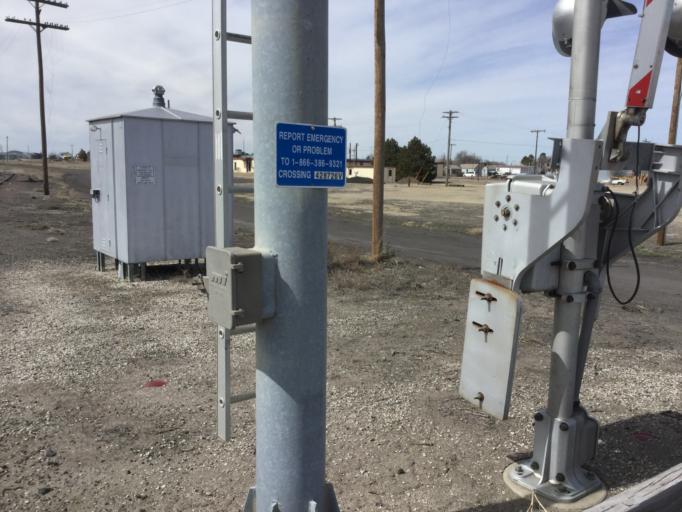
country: US
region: Kansas
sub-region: Greeley County
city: Tribune
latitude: 38.4731
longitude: -101.7902
